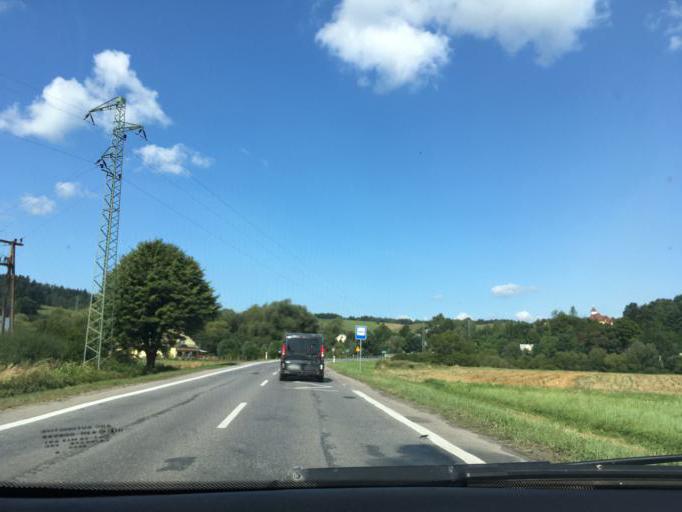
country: PL
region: Subcarpathian Voivodeship
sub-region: Powiat leski
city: Lesko
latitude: 49.4935
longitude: 22.3134
